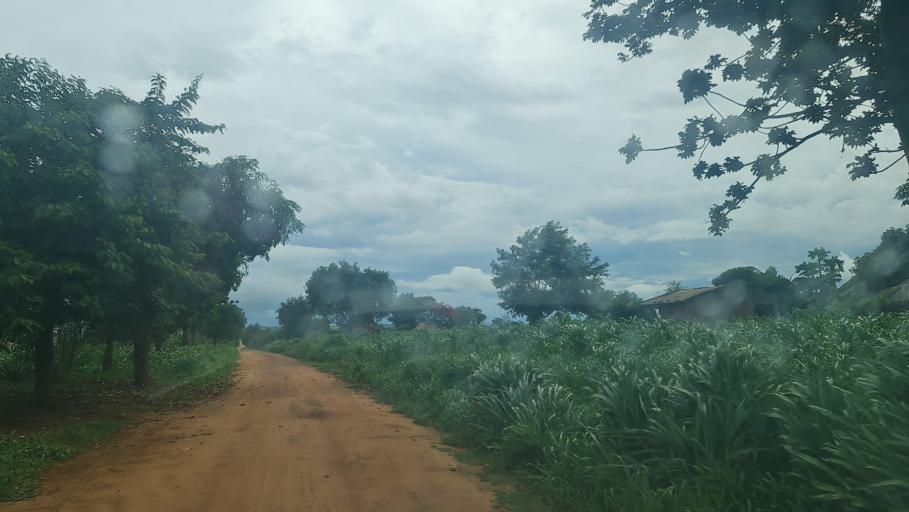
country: MW
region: Southern Region
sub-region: Nsanje District
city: Nsanje
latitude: -17.3957
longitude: 35.5811
